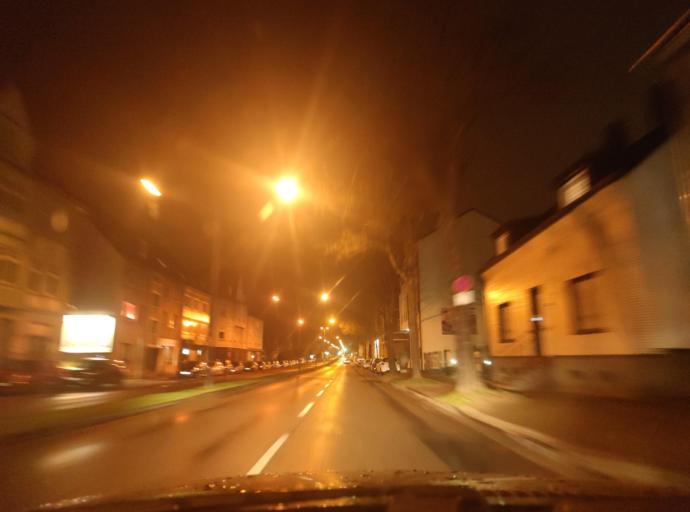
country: DE
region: North Rhine-Westphalia
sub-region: Regierungsbezirk Munster
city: Gelsenkirchen
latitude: 51.4529
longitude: 7.1035
